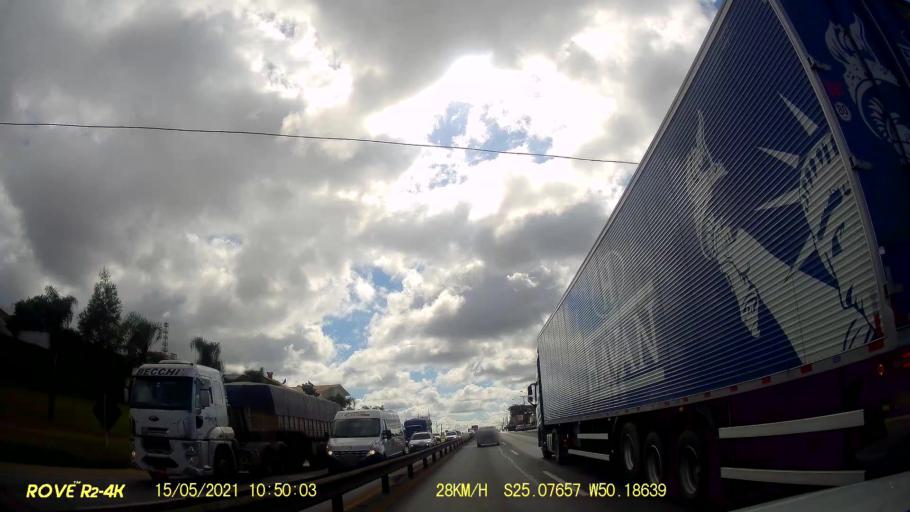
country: BR
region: Parana
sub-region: Ponta Grossa
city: Ponta Grossa
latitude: -25.0767
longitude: -50.1864
